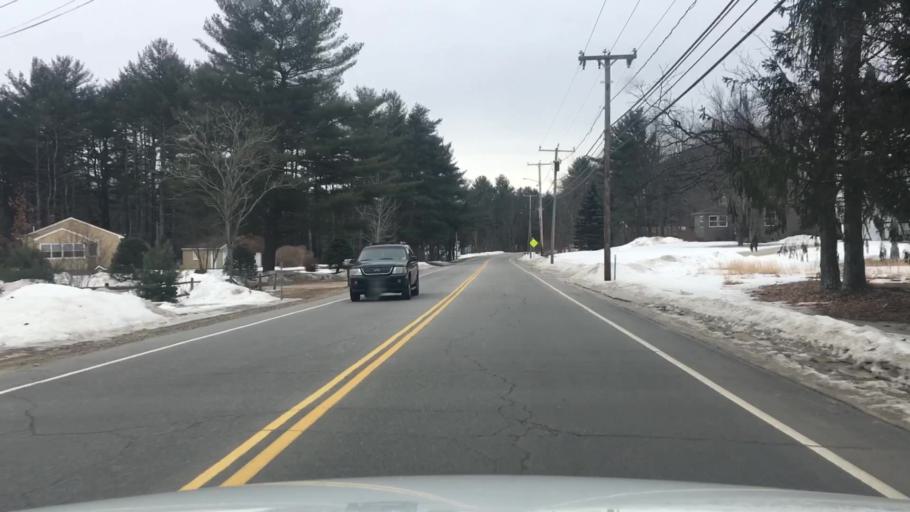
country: US
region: New Hampshire
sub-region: Strafford County
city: Rochester
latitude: 43.3712
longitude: -70.9838
